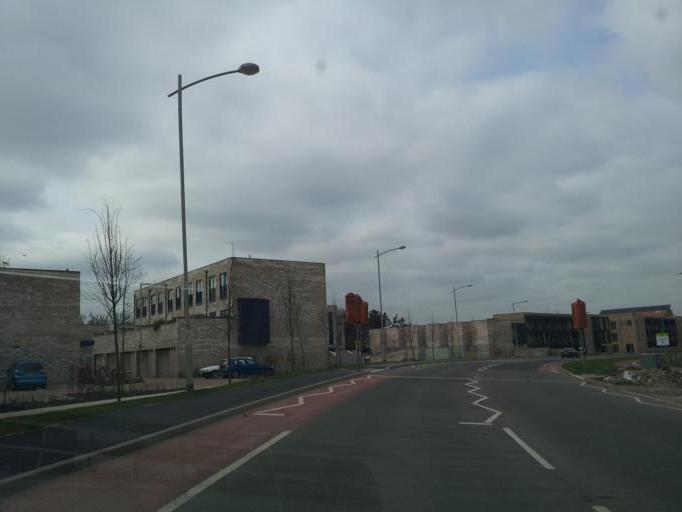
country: GB
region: England
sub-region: Cambridgeshire
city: Cambridge
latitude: 52.1666
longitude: 0.1233
